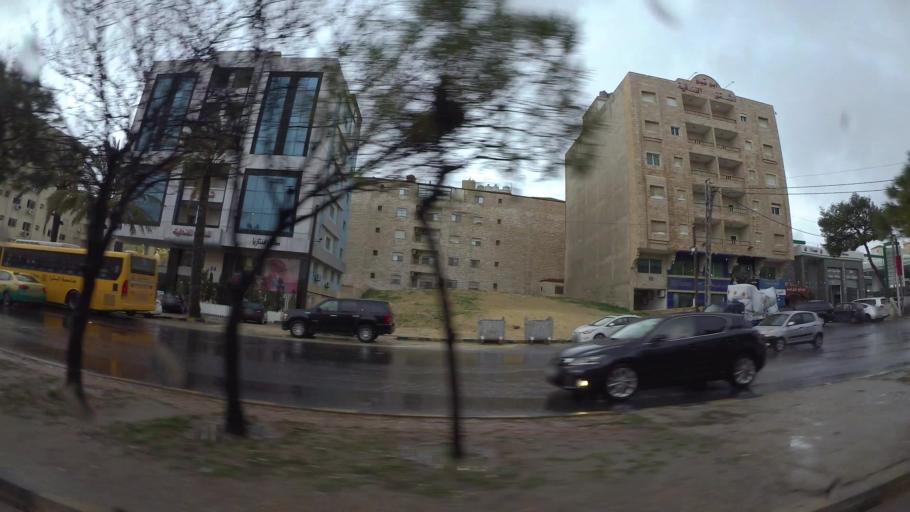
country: JO
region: Amman
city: Al Jubayhah
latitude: 32.0290
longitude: 35.8703
